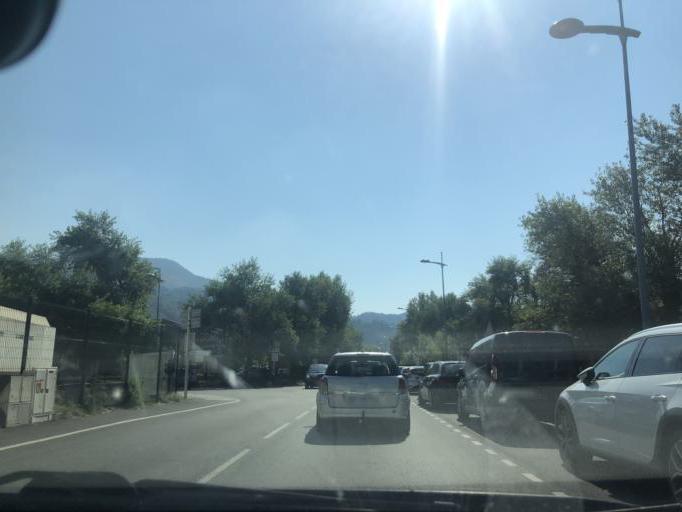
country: FR
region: Provence-Alpes-Cote d'Azur
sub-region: Departement des Alpes-Maritimes
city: Castagniers
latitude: 43.7872
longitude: 7.2092
